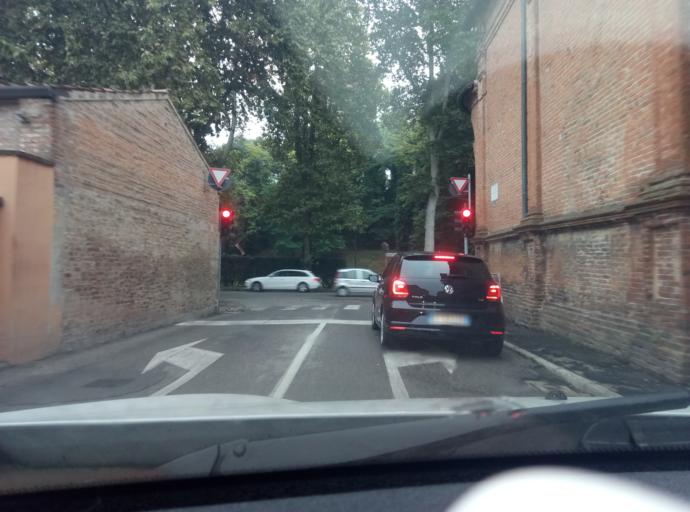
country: IT
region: Emilia-Romagna
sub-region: Provincia di Ferrara
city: Ferrara
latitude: 44.8276
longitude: 11.6310
